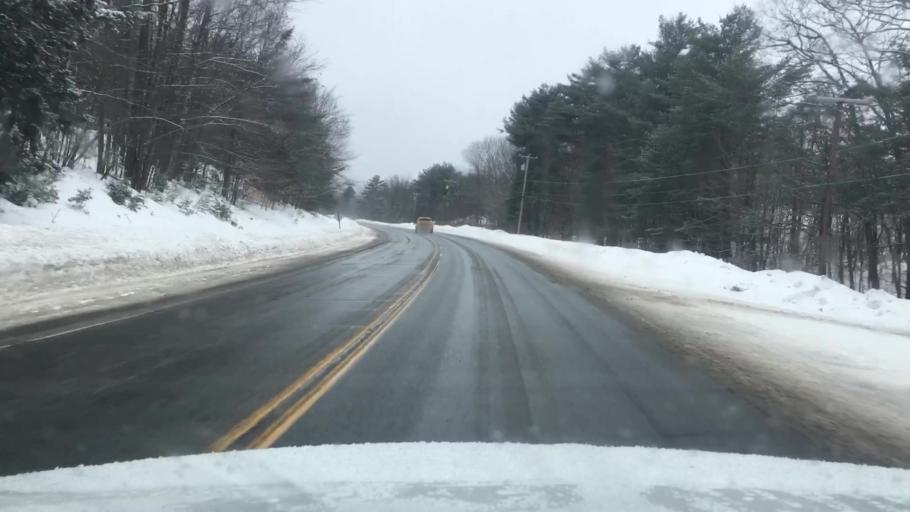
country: US
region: Maine
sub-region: Oxford County
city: Peru
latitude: 44.4870
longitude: -70.3619
